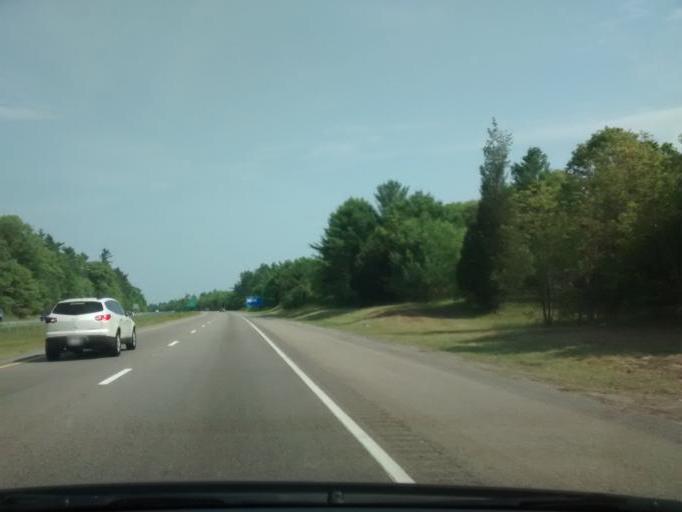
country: US
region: Massachusetts
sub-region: Plymouth County
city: Middleborough Center
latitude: 41.8601
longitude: -70.8778
